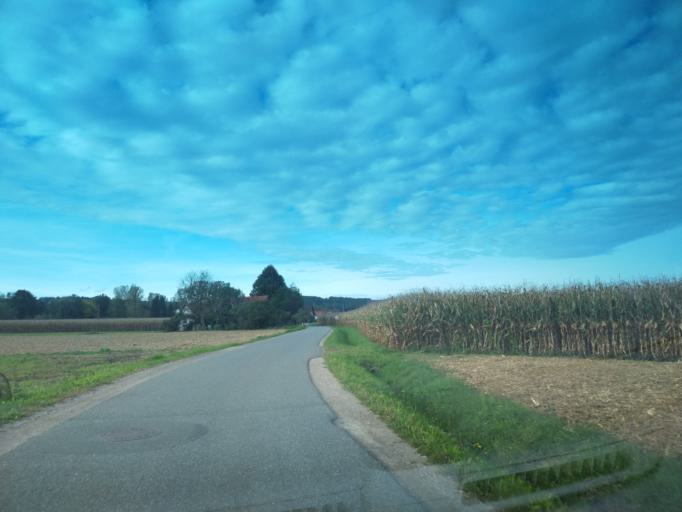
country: AT
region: Styria
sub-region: Politischer Bezirk Leibnitz
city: Sankt Johann im Saggautal
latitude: 46.6924
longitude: 15.3935
